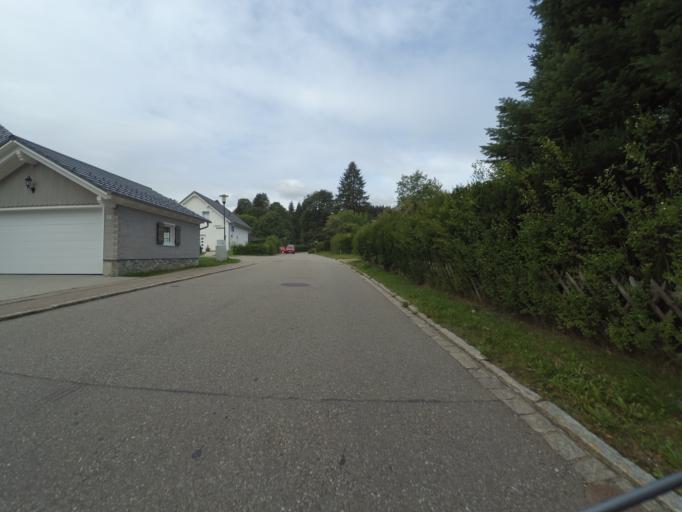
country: DE
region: Baden-Wuerttemberg
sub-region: Freiburg Region
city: Hinterzarten
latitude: 47.9071
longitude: 8.0980
